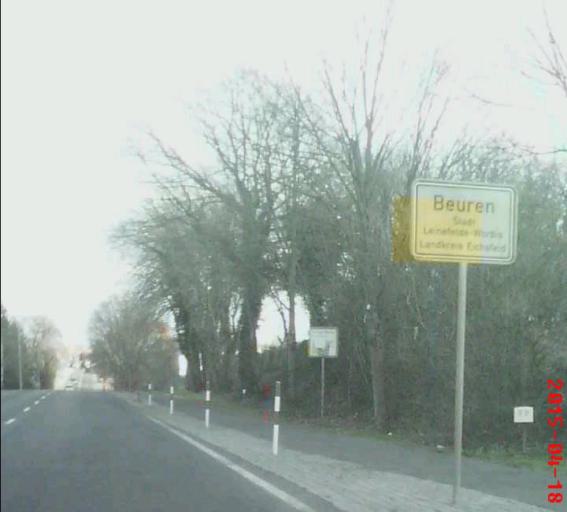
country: DE
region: Thuringia
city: Kreuzebra
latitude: 51.3786
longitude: 10.2707
